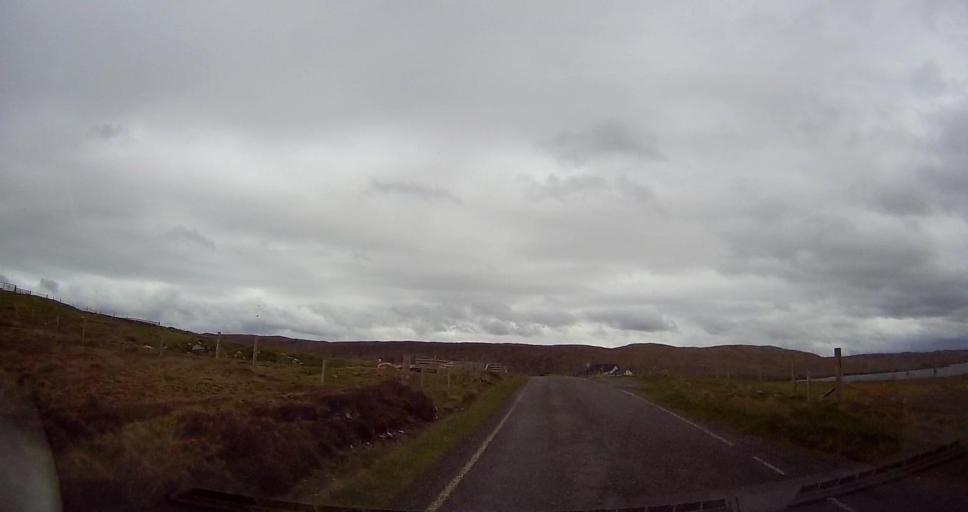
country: GB
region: Scotland
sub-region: Shetland Islands
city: Lerwick
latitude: 60.4853
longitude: -1.4813
